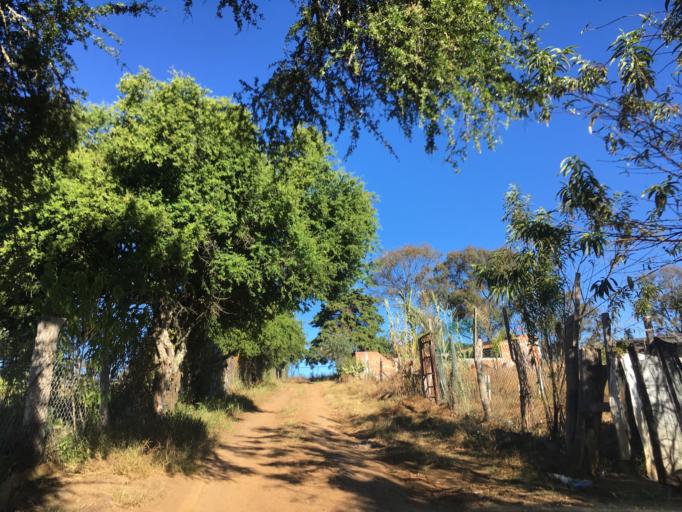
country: MX
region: Michoacan
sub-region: Morelia
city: Montana Monarca (Punta Altozano)
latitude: 19.6561
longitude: -101.1492
